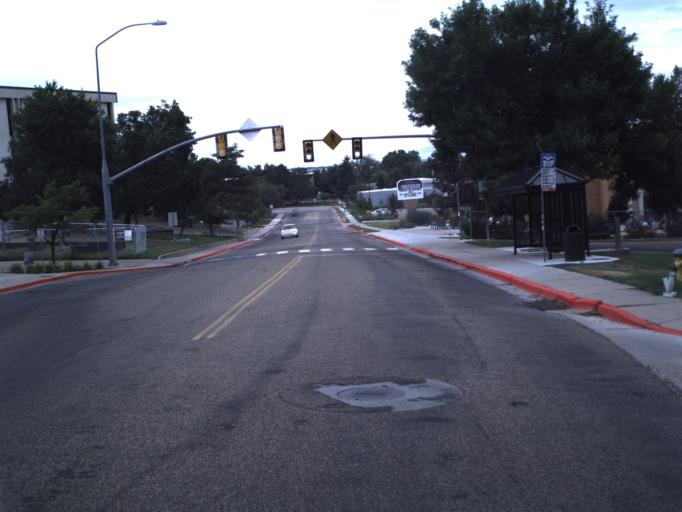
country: US
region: Utah
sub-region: Weber County
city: South Ogden
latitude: 41.1948
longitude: -111.9446
